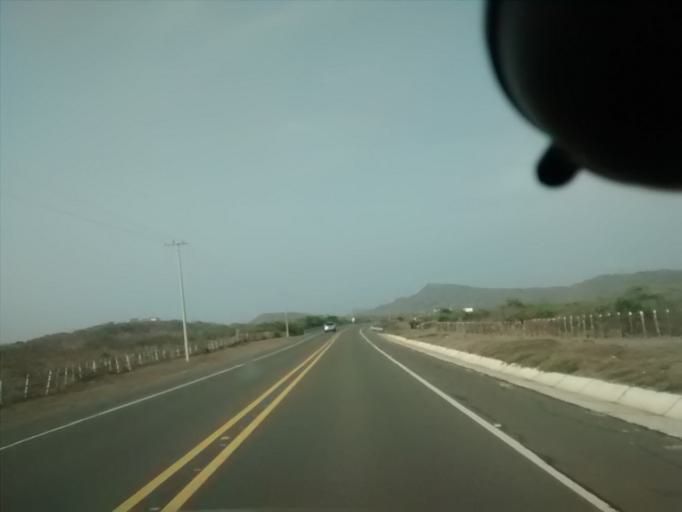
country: CO
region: Atlantico
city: Juan de Acosta
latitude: 10.8618
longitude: -75.1060
